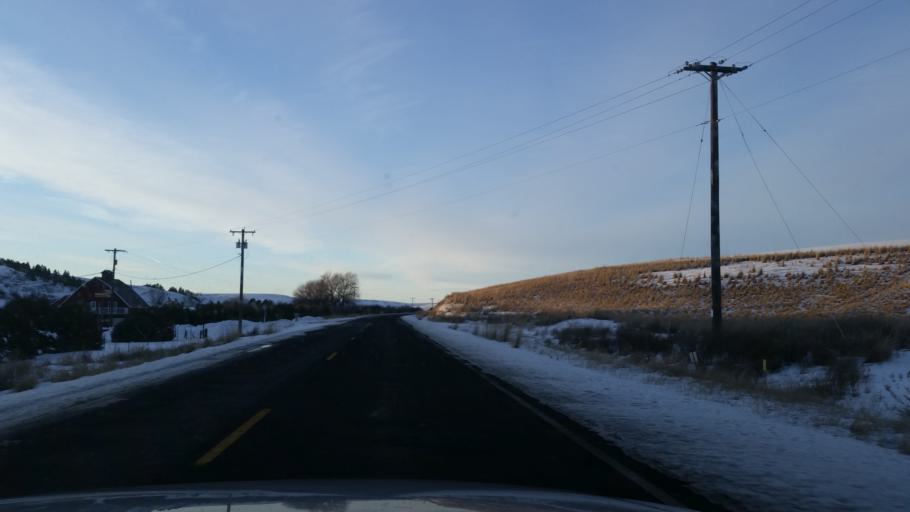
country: US
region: Washington
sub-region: Whitman County
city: Colfax
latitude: 47.1004
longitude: -117.6092
